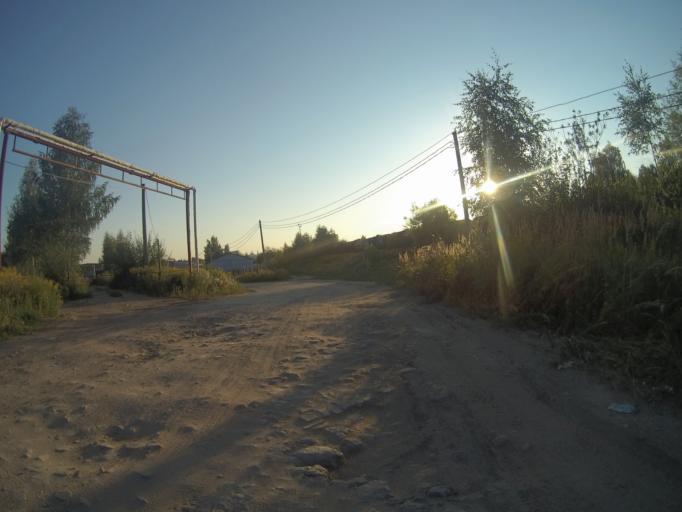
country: RU
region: Vladimir
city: Kommunar
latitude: 56.1380
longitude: 40.4550
